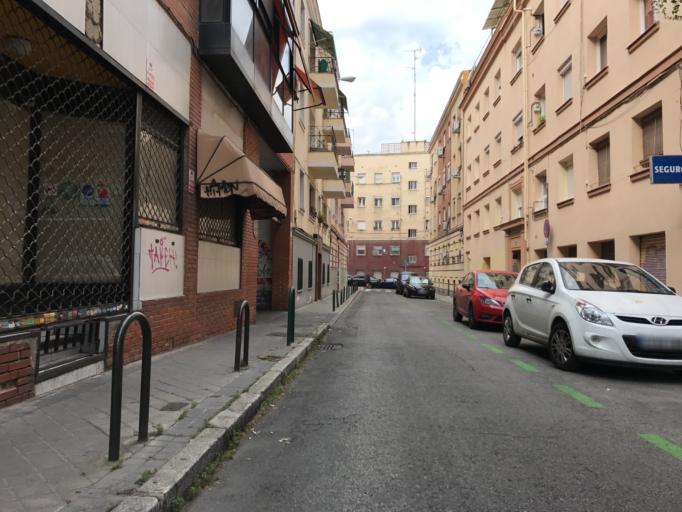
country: ES
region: Madrid
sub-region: Provincia de Madrid
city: Salamanca
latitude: 40.4412
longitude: -3.6751
